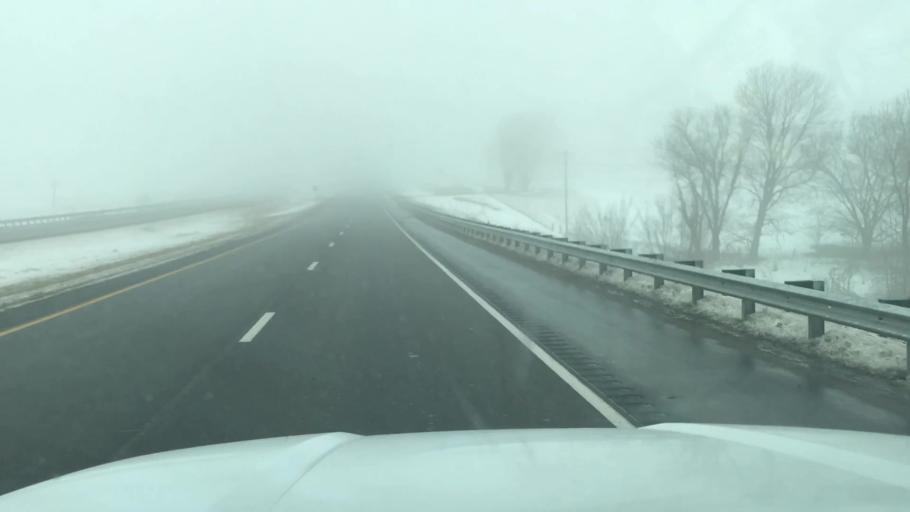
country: US
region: Missouri
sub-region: Clinton County
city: Cameron
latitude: 39.7541
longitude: -94.2637
